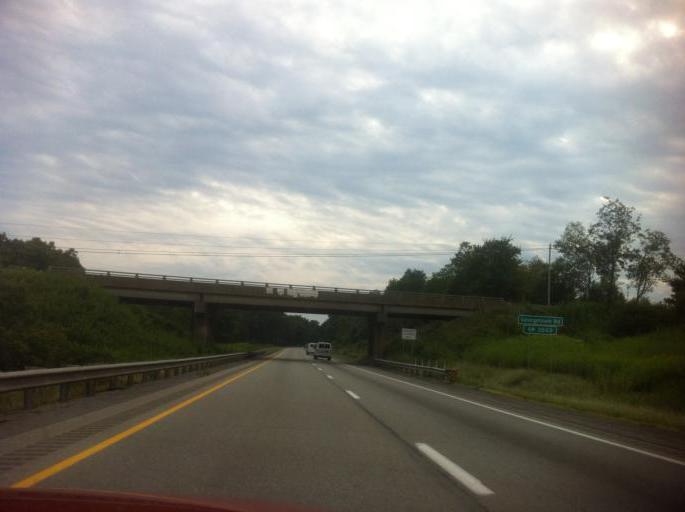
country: US
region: Pennsylvania
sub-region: Mercer County
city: Grove City
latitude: 41.2031
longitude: -79.9351
